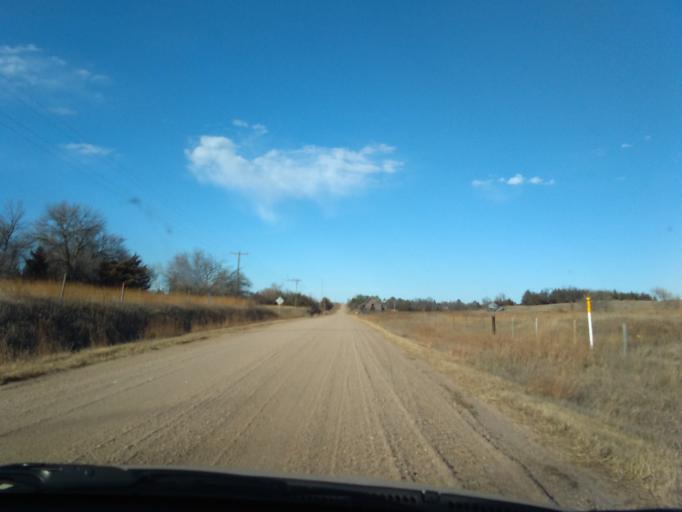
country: US
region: Nebraska
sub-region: Franklin County
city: Franklin
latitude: 40.2933
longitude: -98.7457
